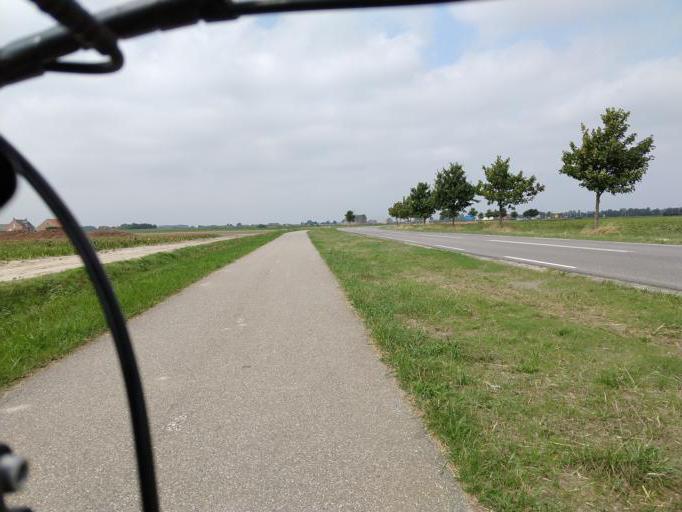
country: NL
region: Zeeland
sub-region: Schouwen-Duiveland
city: Bruinisse
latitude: 51.6560
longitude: 4.0802
